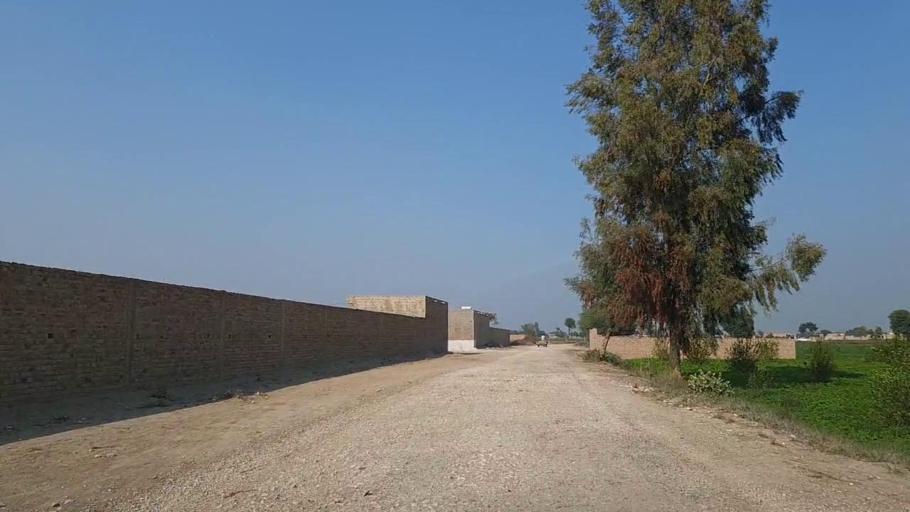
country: PK
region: Sindh
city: Moro
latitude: 26.6889
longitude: 67.9482
